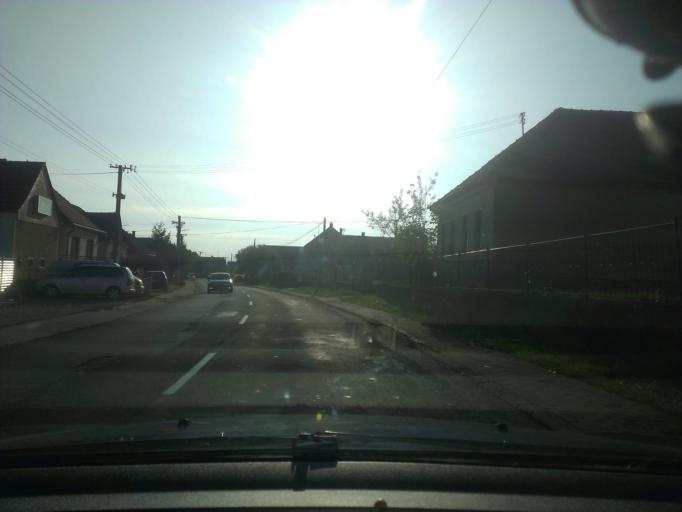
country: SK
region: Trnavsky
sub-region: Okres Trnava
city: Piestany
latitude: 48.5244
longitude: 17.9660
